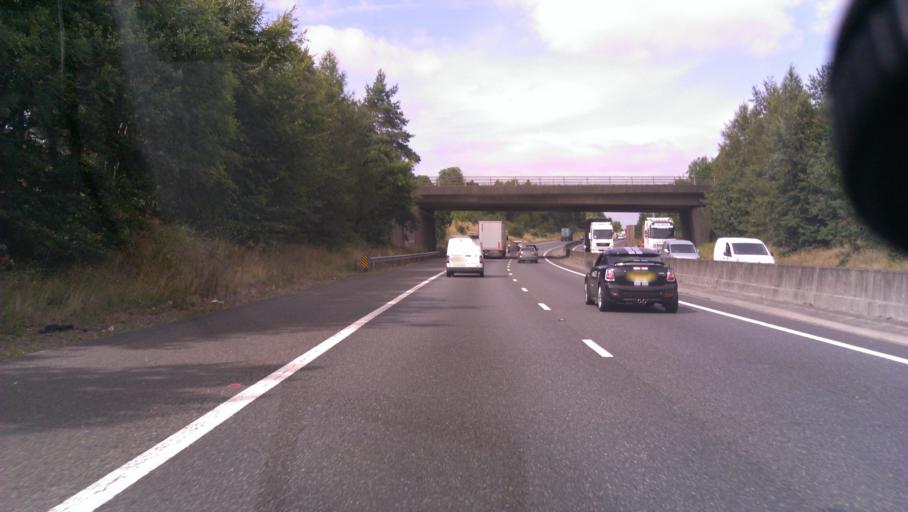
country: GB
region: England
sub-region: Essex
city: Elsenham
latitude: 51.9588
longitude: 0.2133
